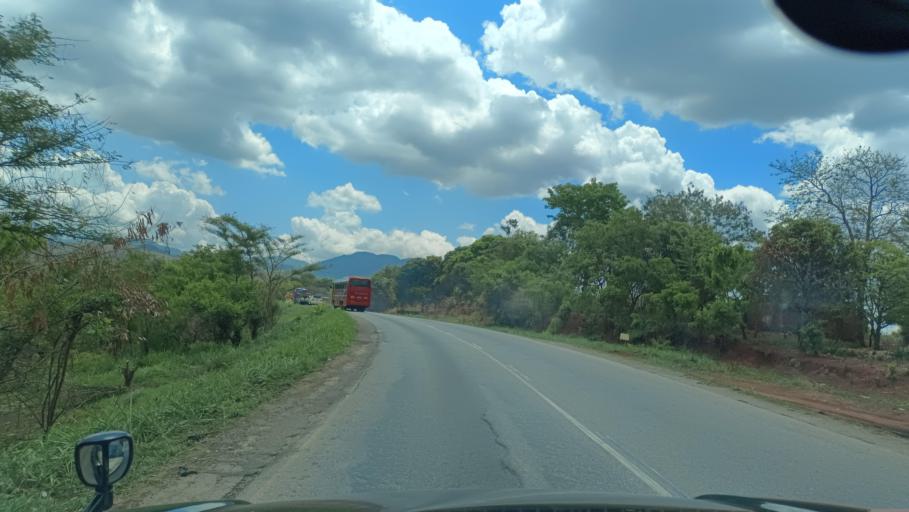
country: TZ
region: Morogoro
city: Mikumi
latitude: -7.4594
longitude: 36.9196
